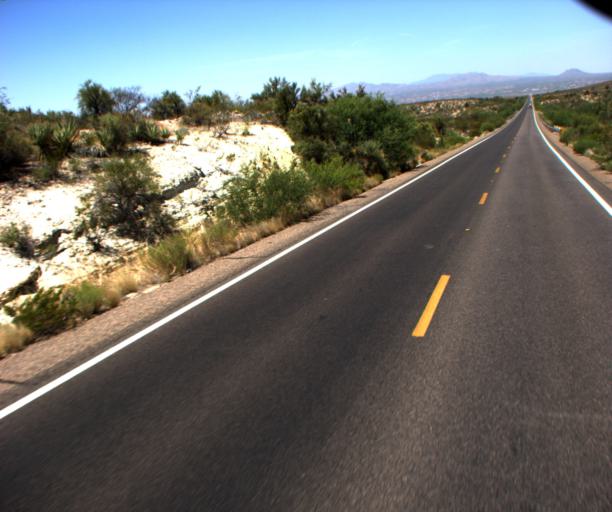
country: US
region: Arizona
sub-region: Gila County
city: Peridot
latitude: 33.2869
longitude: -110.3822
